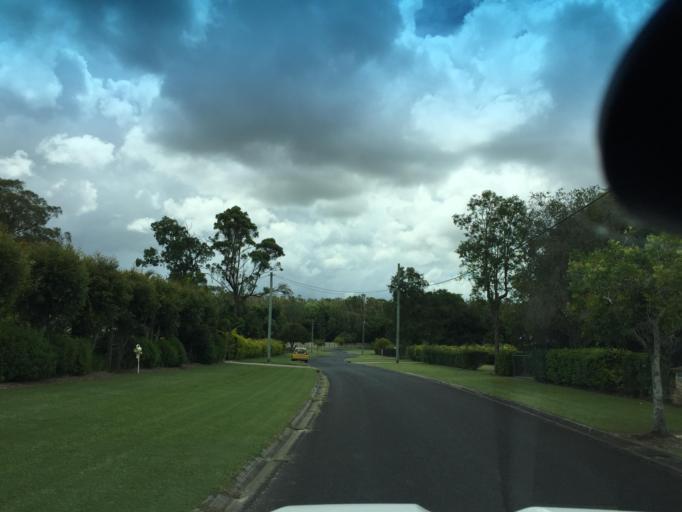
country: AU
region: Queensland
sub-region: Moreton Bay
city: Caboolture
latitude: -27.0413
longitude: 152.9230
